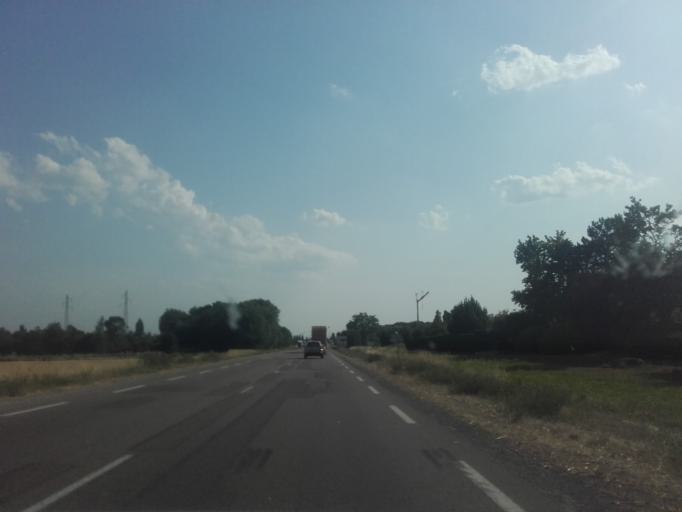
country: FR
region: Bourgogne
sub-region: Departement de la Cote-d'Or
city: Beaune
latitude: 47.0126
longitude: 4.8548
